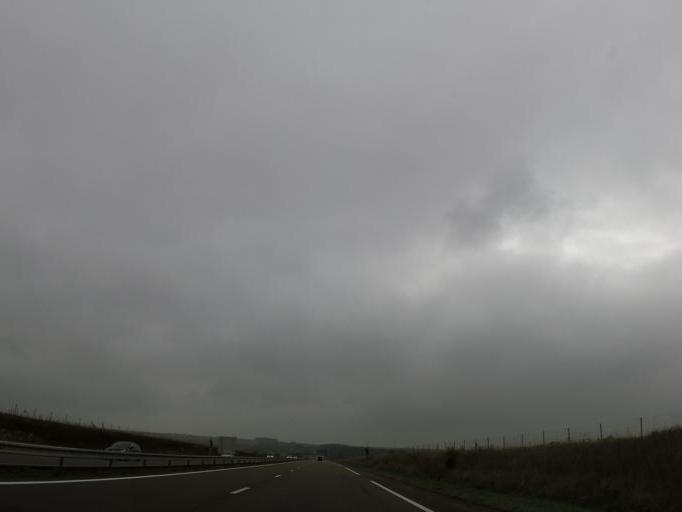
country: FR
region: Champagne-Ardenne
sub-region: Departement de la Marne
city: Mourmelon-le-Grand
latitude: 49.0678
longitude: 4.2718
